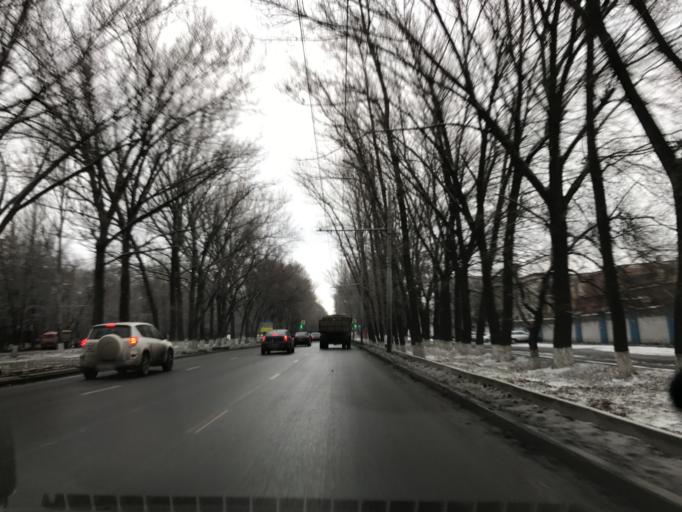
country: RU
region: Rostov
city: Aksay
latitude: 47.2617
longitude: 39.8086
